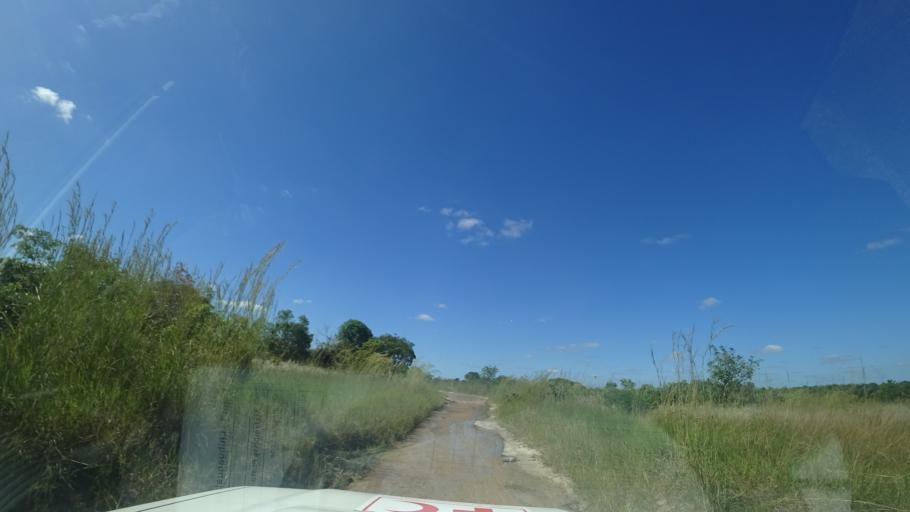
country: MZ
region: Sofala
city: Dondo
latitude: -19.4765
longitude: 34.6290
